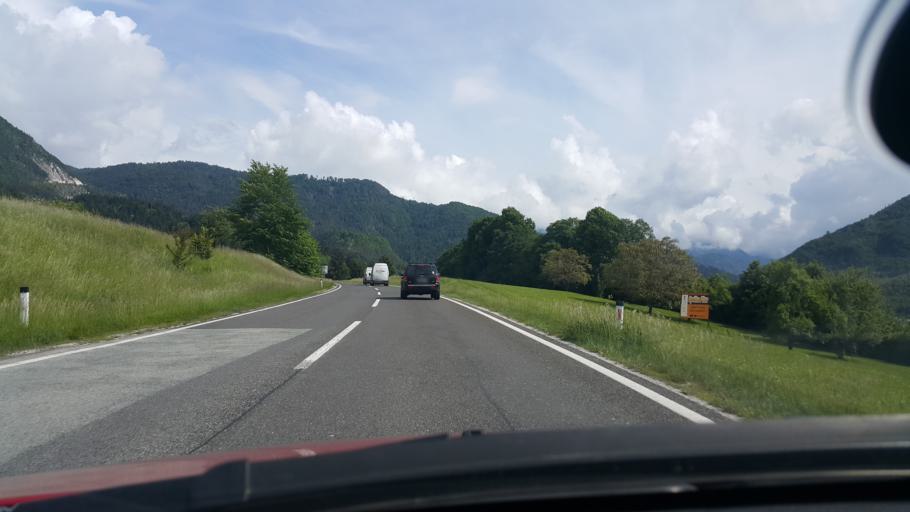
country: SI
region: Trzic
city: Bistrica pri Trzicu
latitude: 46.3415
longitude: 14.2861
